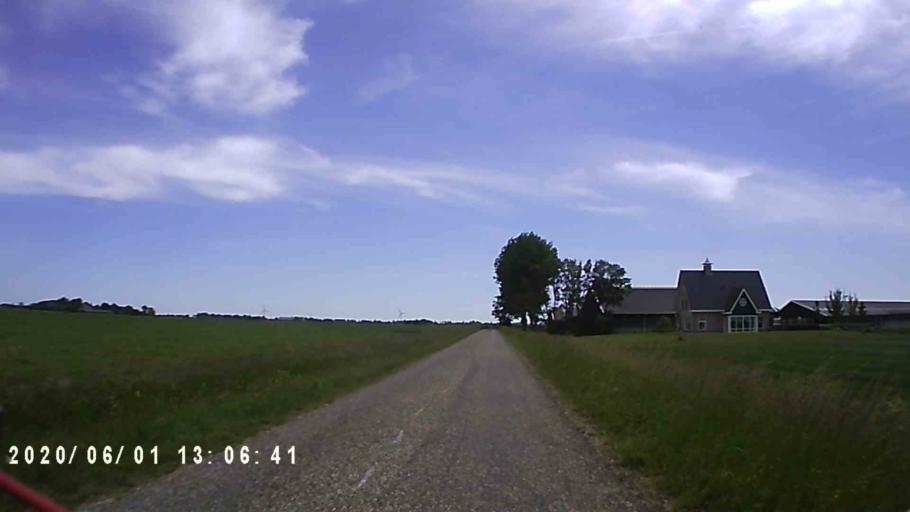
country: NL
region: Friesland
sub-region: Gemeente Franekeradeel
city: Tzum
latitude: 53.1339
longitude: 5.5522
